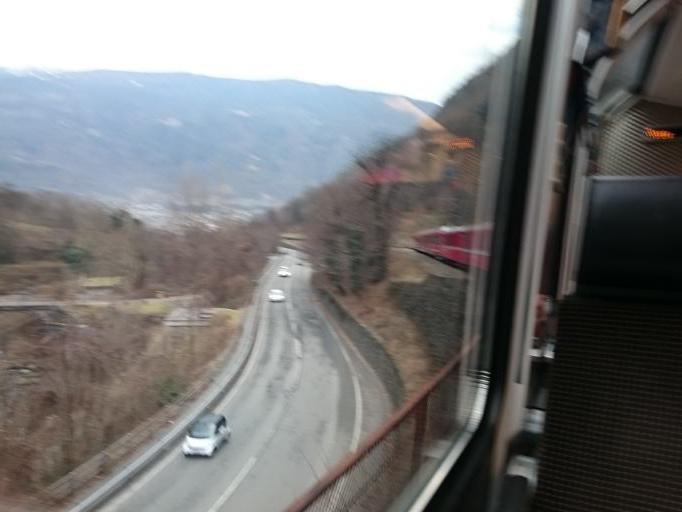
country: IT
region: Lombardy
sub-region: Provincia di Sondrio
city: Tirano
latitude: 46.2271
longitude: 10.1461
